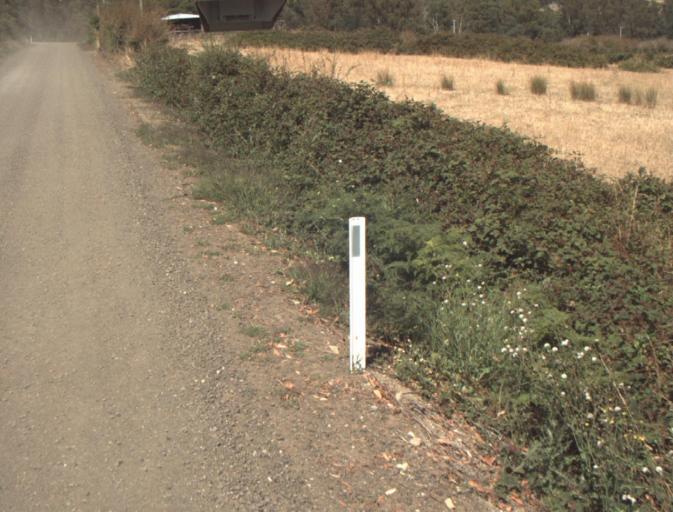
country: AU
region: Tasmania
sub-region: Launceston
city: Mayfield
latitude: -41.2582
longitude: 147.1693
